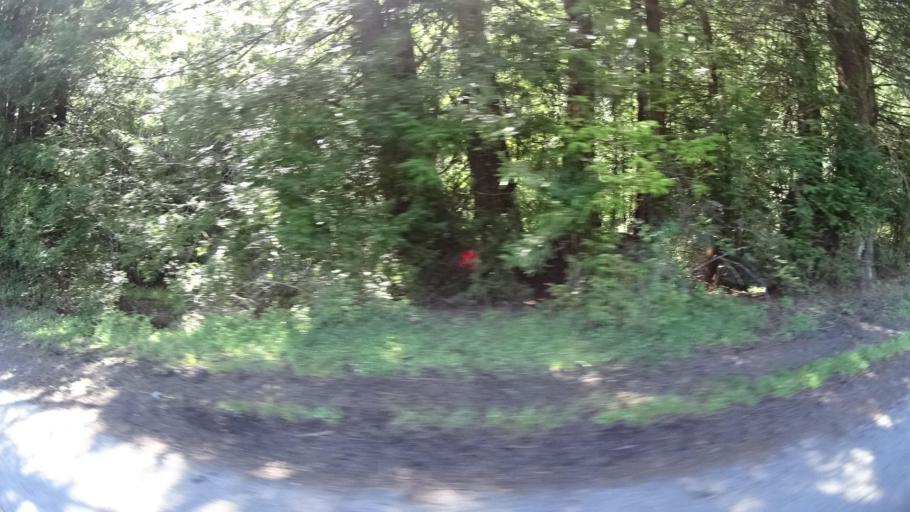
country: US
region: California
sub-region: Humboldt County
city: Fortuna
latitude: 40.5246
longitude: -124.1904
